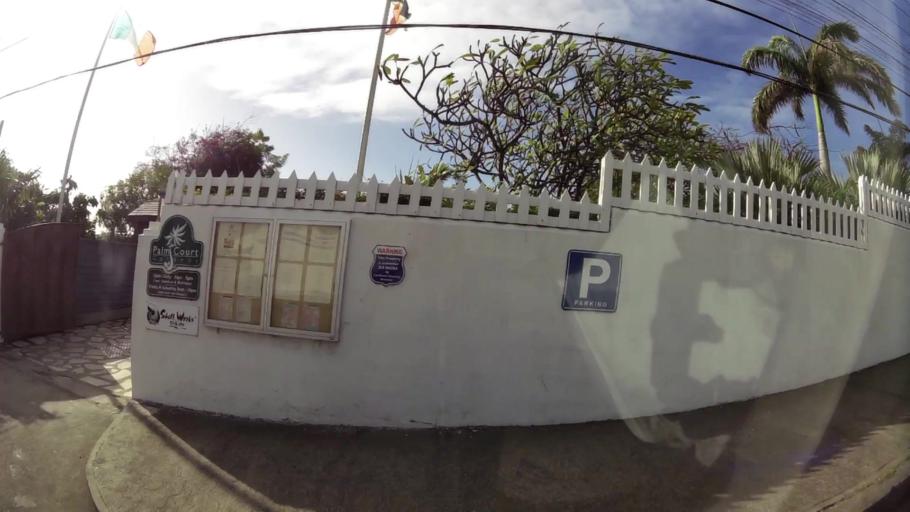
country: KN
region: Saint George Basseterre
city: Basseterre
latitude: 17.2925
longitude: -62.7333
